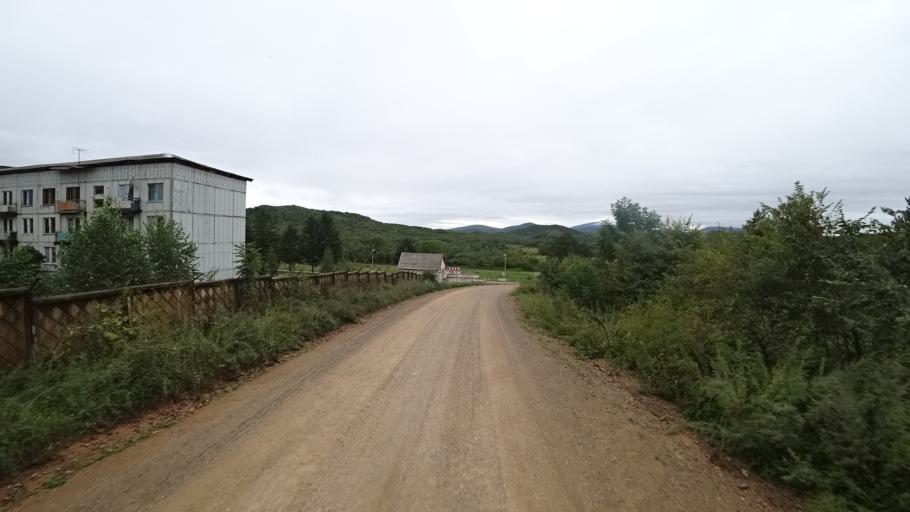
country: RU
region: Primorskiy
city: Rettikhovka
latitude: 44.1718
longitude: 132.8801
